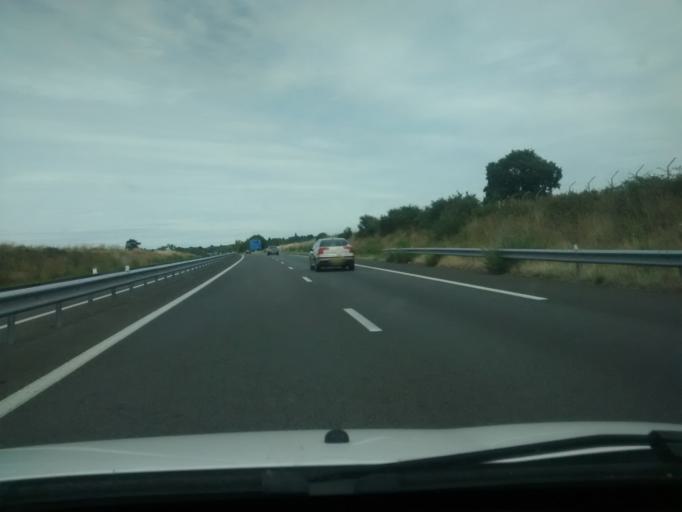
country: FR
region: Brittany
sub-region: Departement d'Ille-et-Vilaine
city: Saint-Sauveur-des-Landes
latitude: 48.3496
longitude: -1.2986
